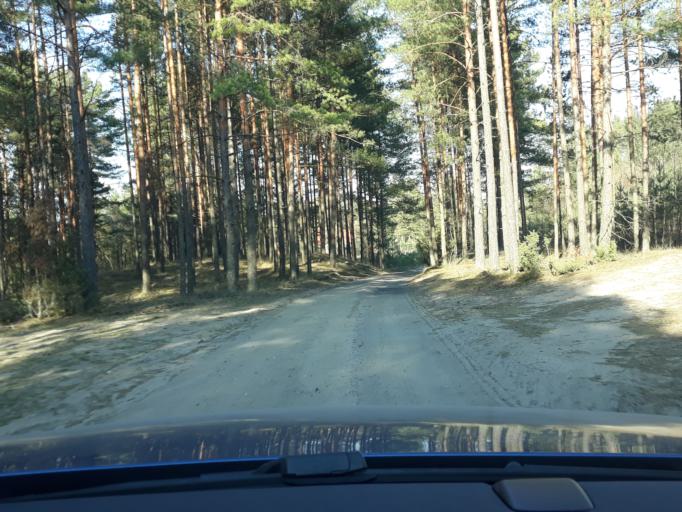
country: PL
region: Pomeranian Voivodeship
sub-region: Powiat bytowski
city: Lipnica
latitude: 53.9223
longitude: 17.4434
